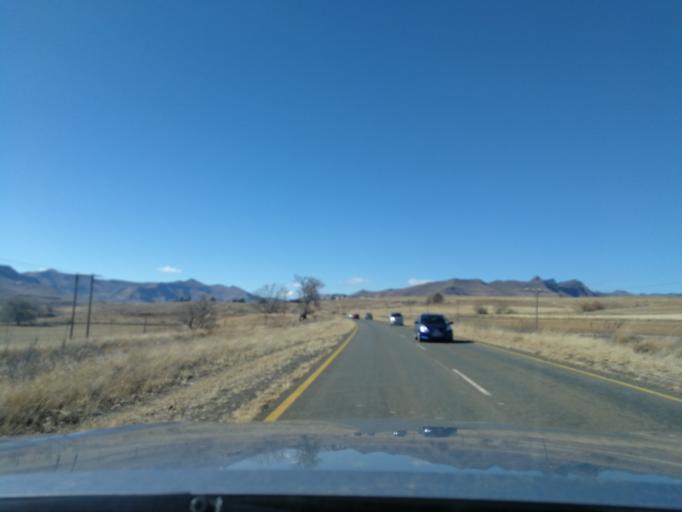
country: ZA
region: Orange Free State
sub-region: Thabo Mofutsanyana District Municipality
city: Phuthaditjhaba
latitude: -28.5267
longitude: 28.4859
